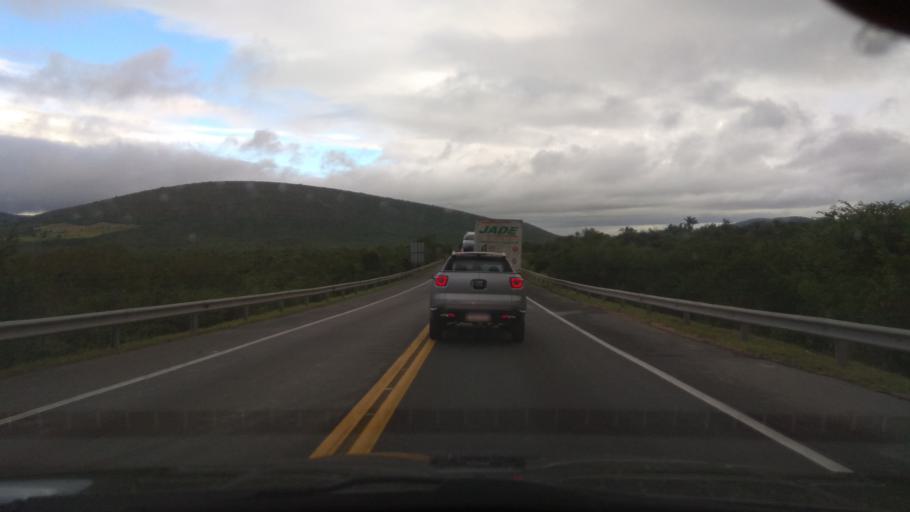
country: BR
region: Bahia
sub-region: Santa Ines
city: Santa Ines
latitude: -13.2606
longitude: -40.0127
